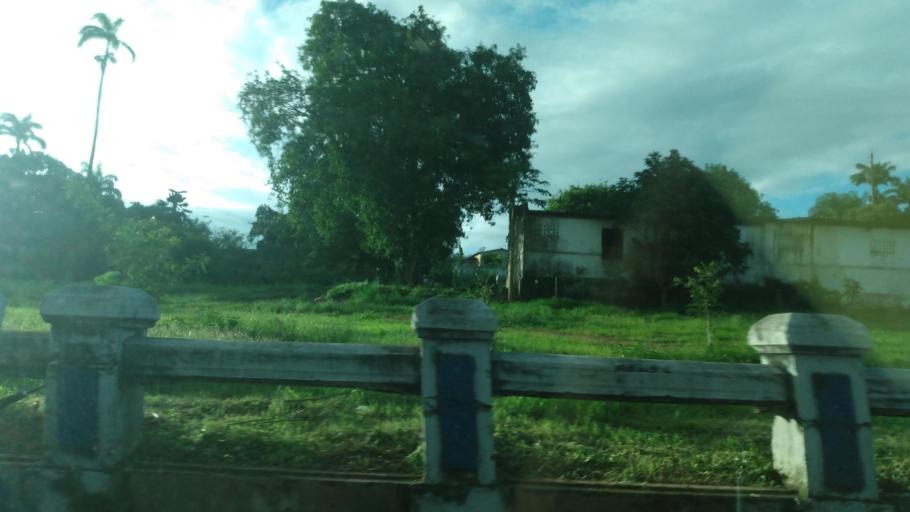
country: BR
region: Pernambuco
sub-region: Palmares
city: Palmares
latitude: -8.6815
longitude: -35.5855
